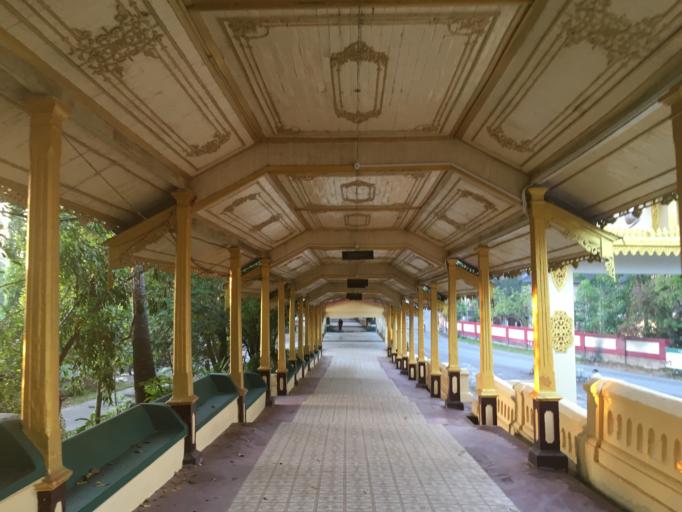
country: MM
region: Mon
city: Mawlamyine
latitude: 16.4916
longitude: 97.6280
